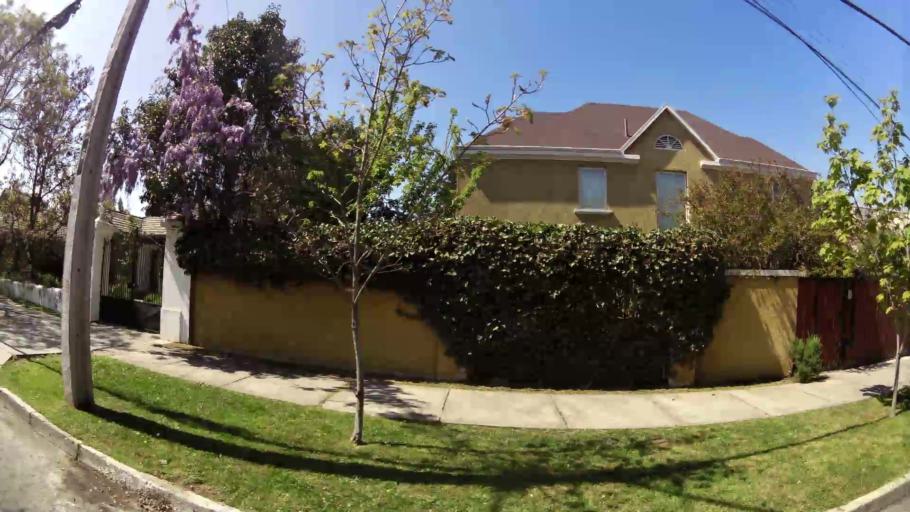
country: CL
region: Santiago Metropolitan
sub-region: Provincia de Santiago
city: Villa Presidente Frei, Nunoa, Santiago, Chile
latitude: -33.4240
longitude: -70.5605
